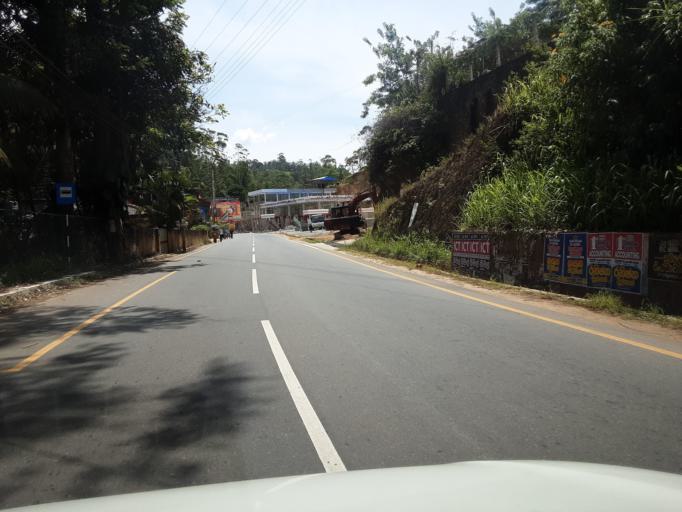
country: LK
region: Central
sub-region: Nuwara Eliya District
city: Nuwara Eliya
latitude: 6.9100
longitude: 80.9059
